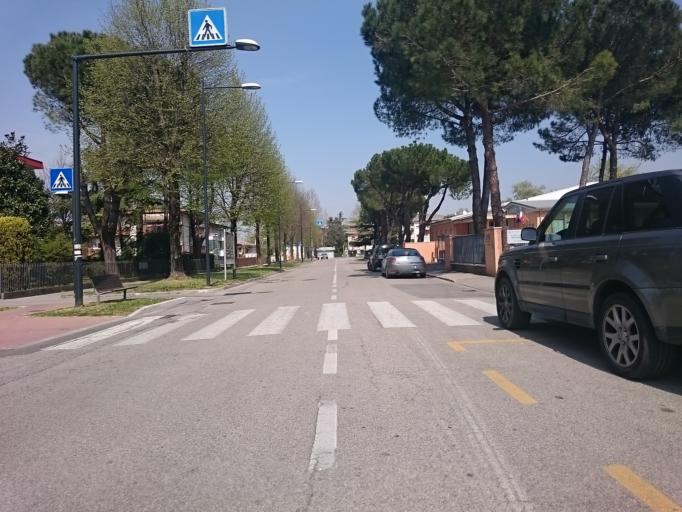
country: IT
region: Veneto
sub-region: Provincia di Padova
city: Caselle
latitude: 45.4130
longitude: 11.8112
